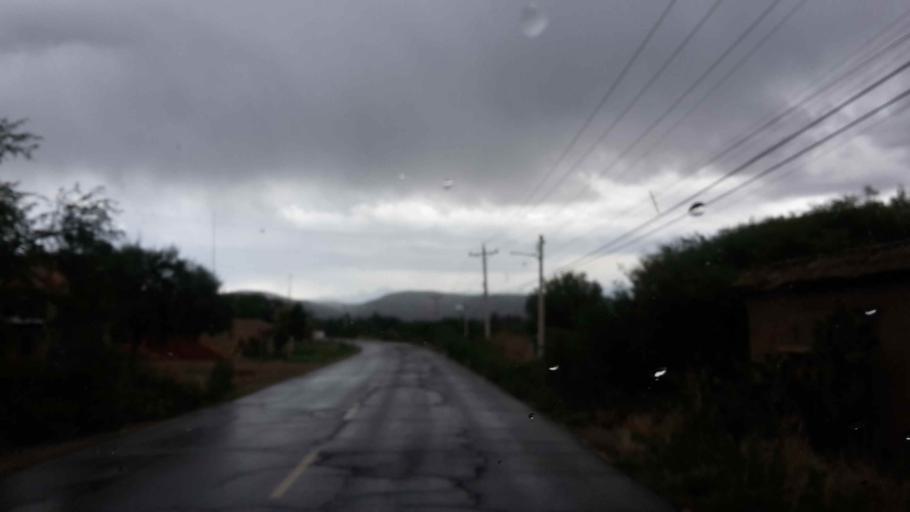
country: BO
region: Cochabamba
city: Tarata
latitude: -17.5749
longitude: -66.0624
